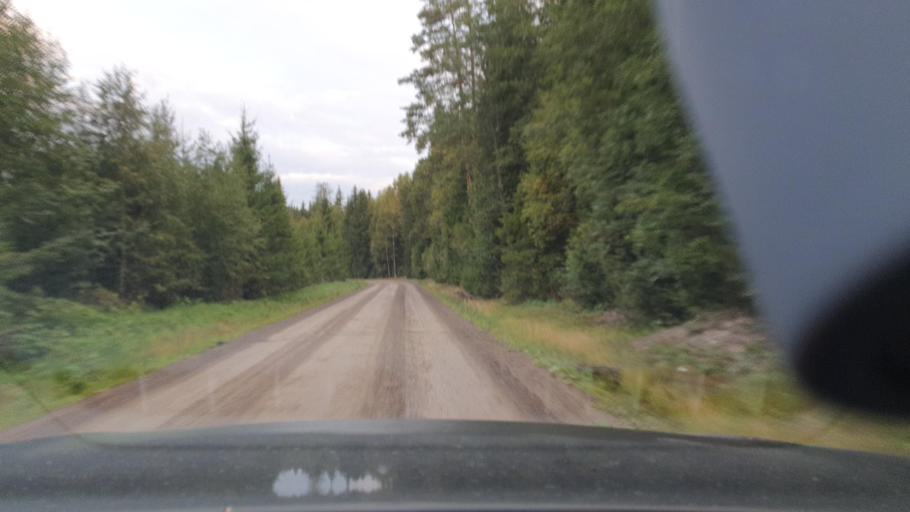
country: SE
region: Vaermland
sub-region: Sunne Kommun
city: Sunne
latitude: 59.8065
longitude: 13.0788
